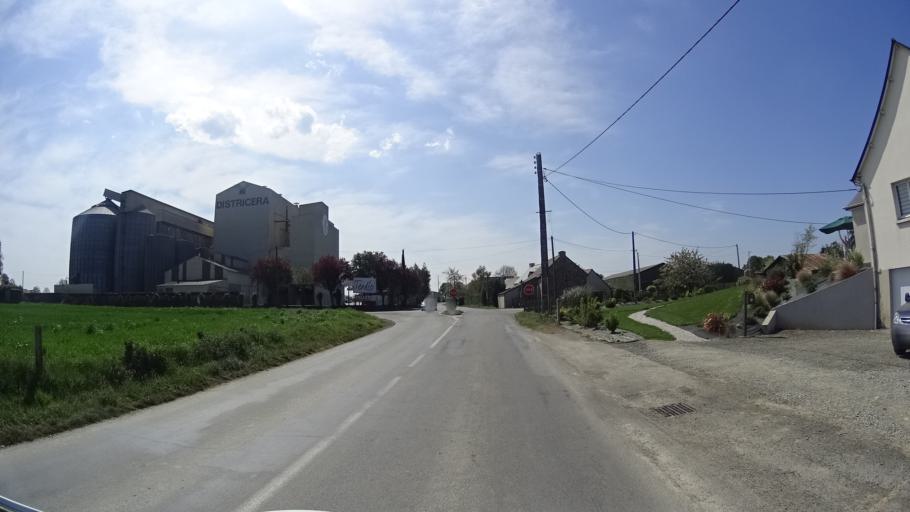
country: FR
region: Brittany
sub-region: Departement d'Ille-et-Vilaine
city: Torce
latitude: 48.0714
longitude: -1.2736
